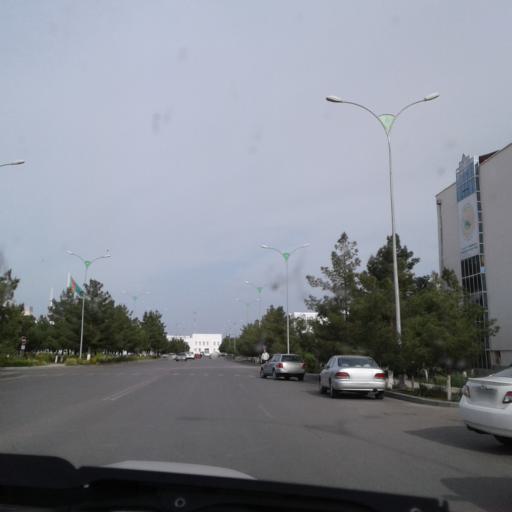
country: TM
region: Mary
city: Mary
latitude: 37.5912
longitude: 61.8385
